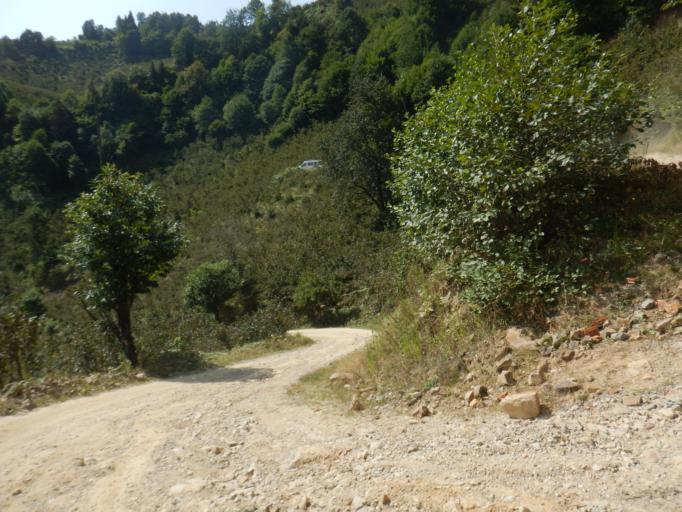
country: TR
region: Ordu
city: Topcam
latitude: 40.7096
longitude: 37.8253
